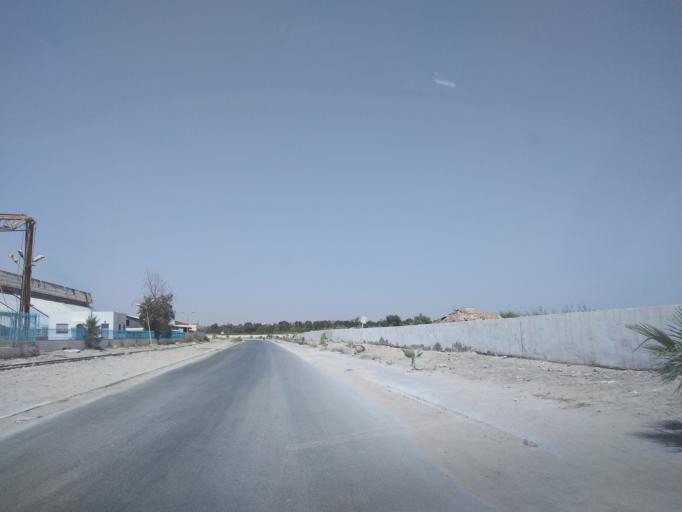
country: TN
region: Safaqis
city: Al Qarmadah
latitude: 34.7308
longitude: 10.7777
